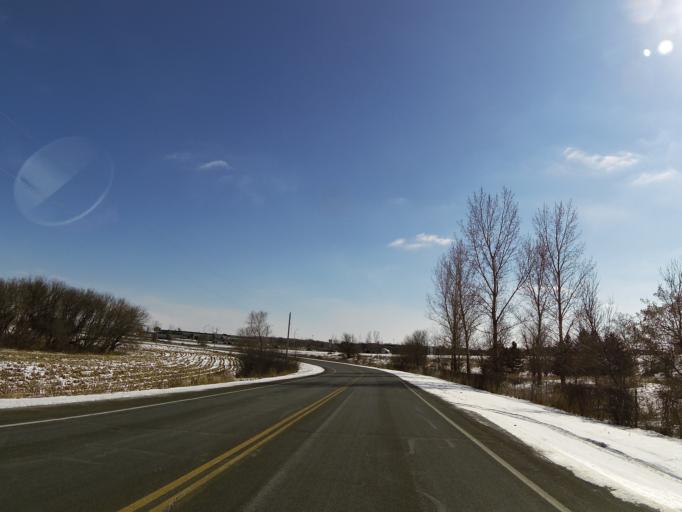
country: US
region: Minnesota
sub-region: Washington County
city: Lake Elmo
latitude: 44.9505
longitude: -92.9008
